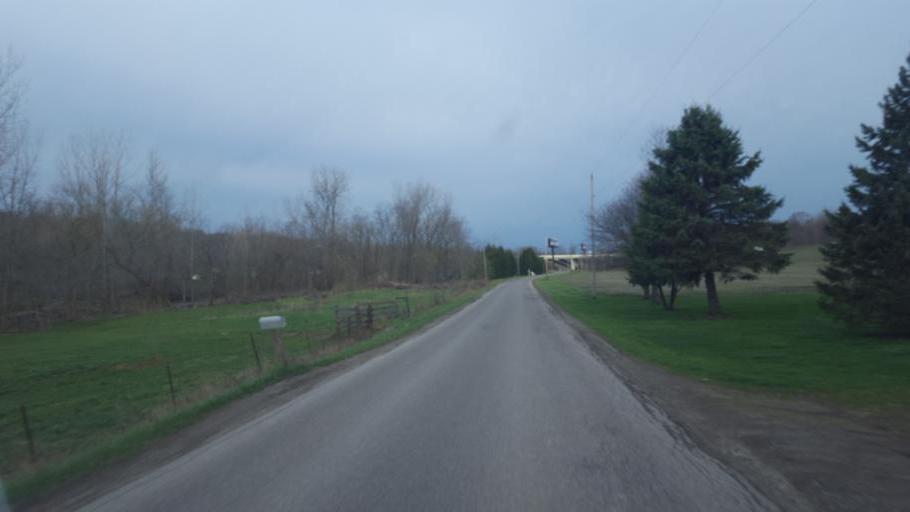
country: US
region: Ohio
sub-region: Knox County
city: Fredericktown
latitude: 40.5450
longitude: -82.6505
